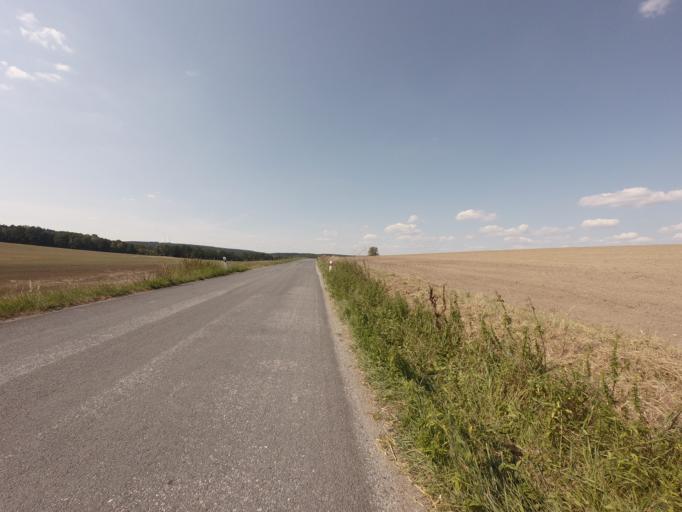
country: CZ
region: Jihocesky
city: Tyn nad Vltavou
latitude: 49.1439
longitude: 14.4466
